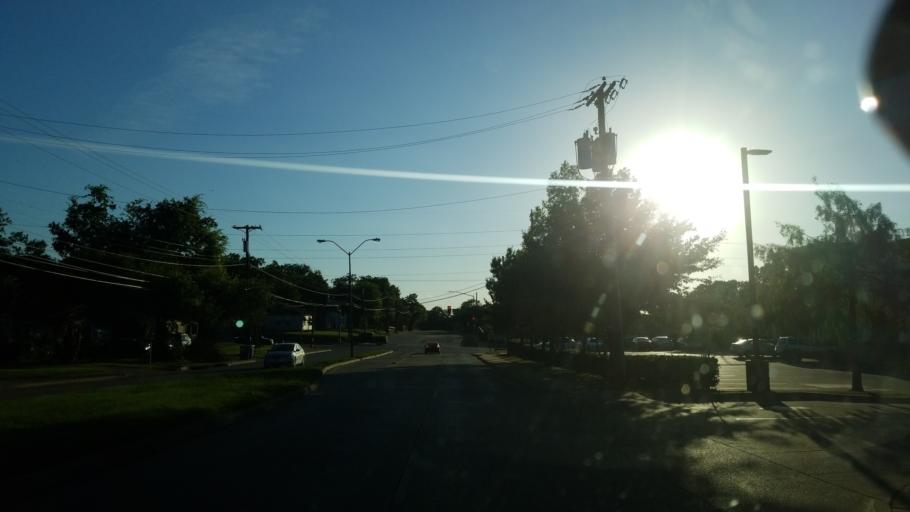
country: US
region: Texas
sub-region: Dallas County
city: Balch Springs
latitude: 32.7781
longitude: -96.6989
